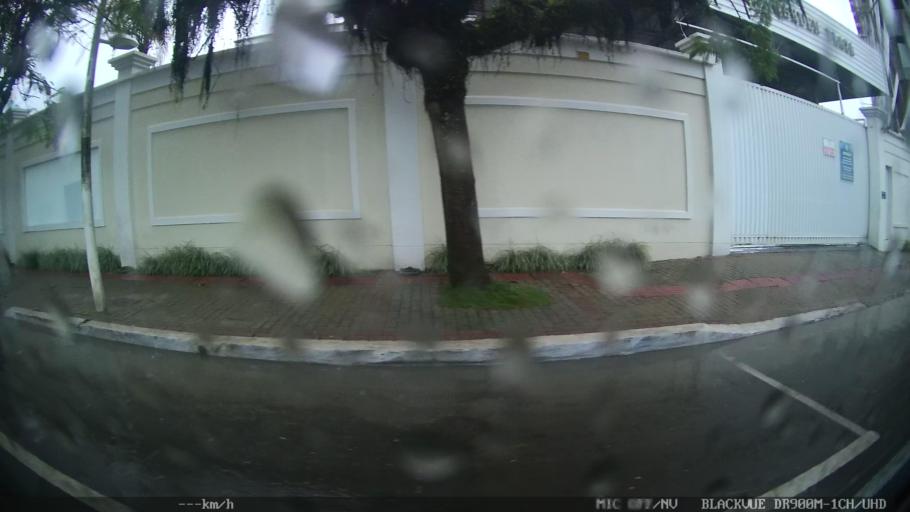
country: BR
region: Santa Catarina
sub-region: Balneario Camboriu
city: Balneario Camboriu
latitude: -27.0071
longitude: -48.6062
